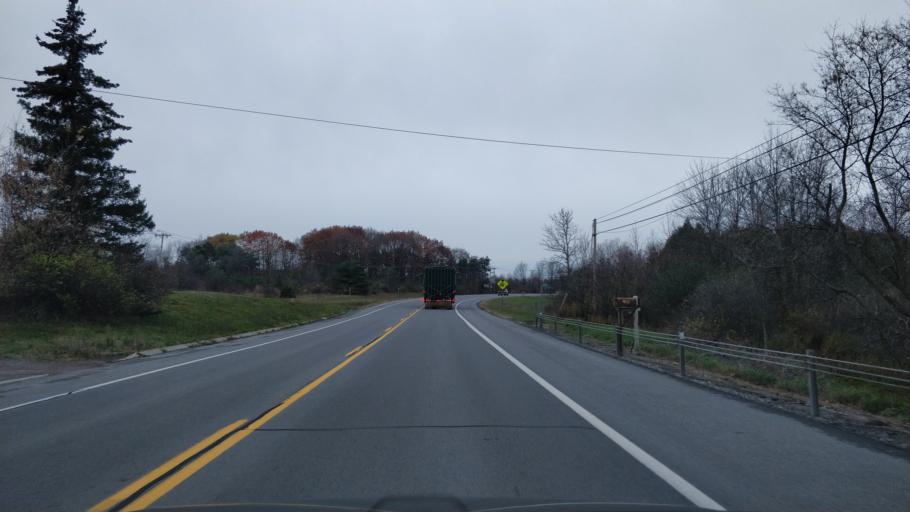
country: CA
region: Ontario
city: Brockville
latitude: 44.6155
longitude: -75.5977
